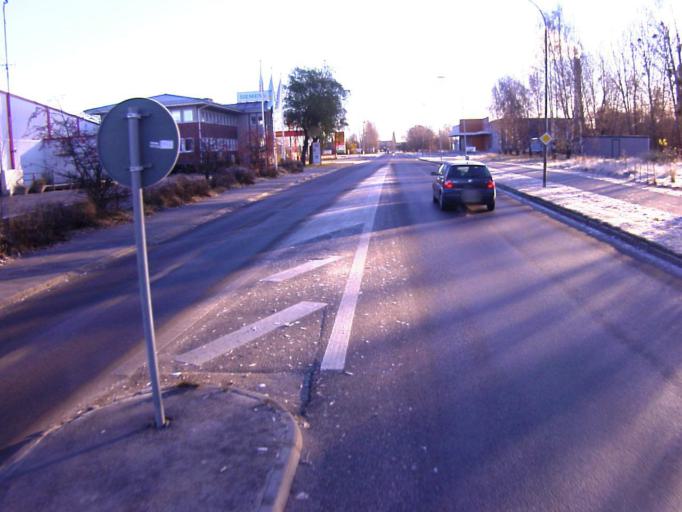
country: SE
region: Soedermanland
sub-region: Eskilstuna Kommun
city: Eskilstuna
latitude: 59.3846
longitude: 16.4915
